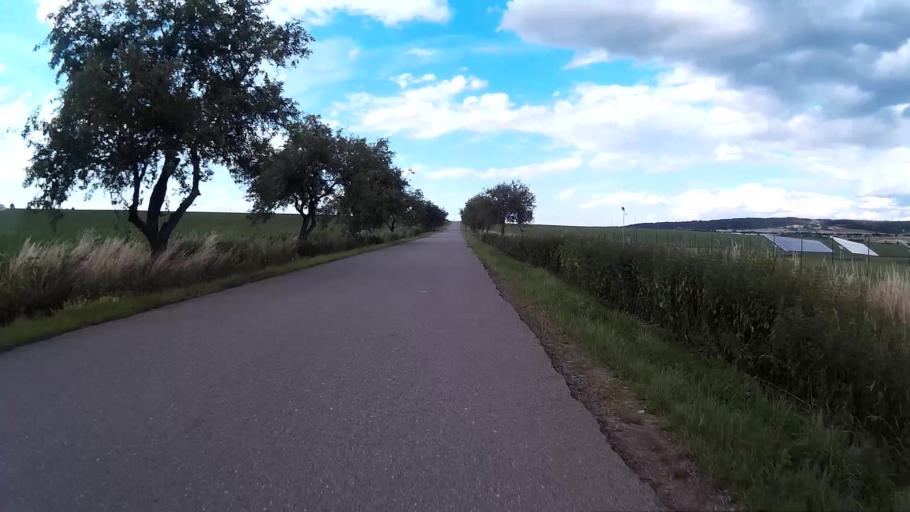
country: CZ
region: South Moravian
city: Ricany
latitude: 49.1993
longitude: 16.4008
